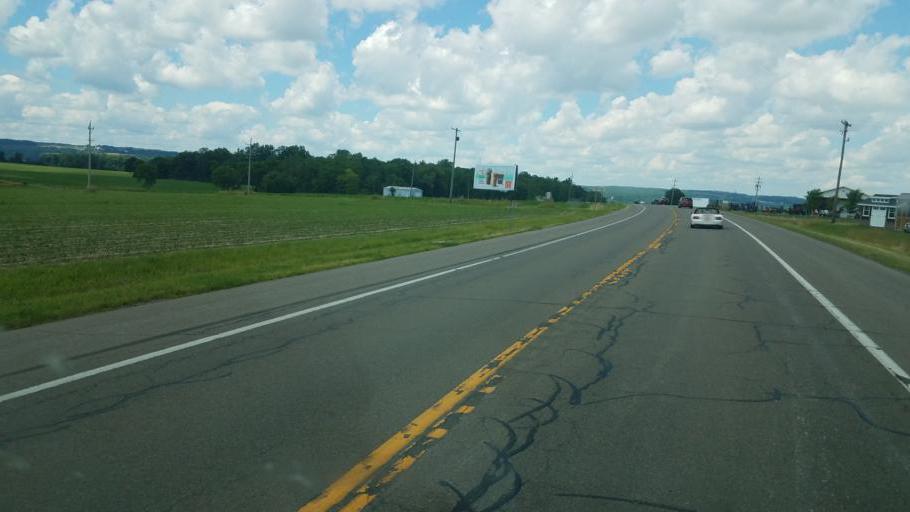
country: US
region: New York
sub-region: Yates County
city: Penn Yan
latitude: 42.6356
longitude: -77.0408
